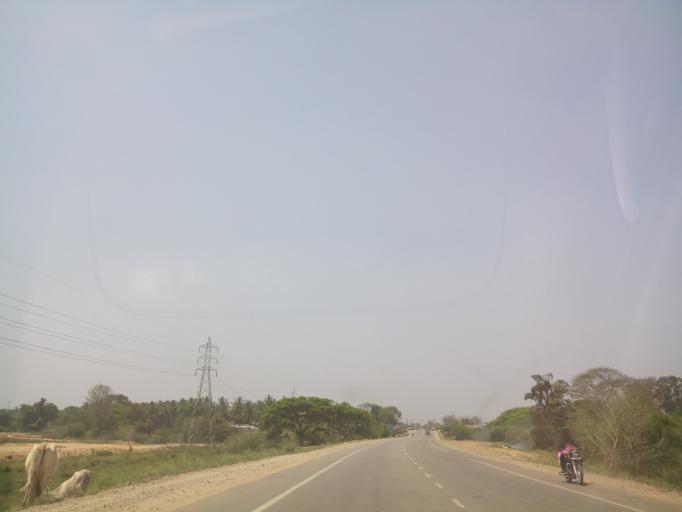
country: IN
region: Karnataka
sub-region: Hassan
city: Hassan
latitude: 12.9910
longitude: 76.0840
